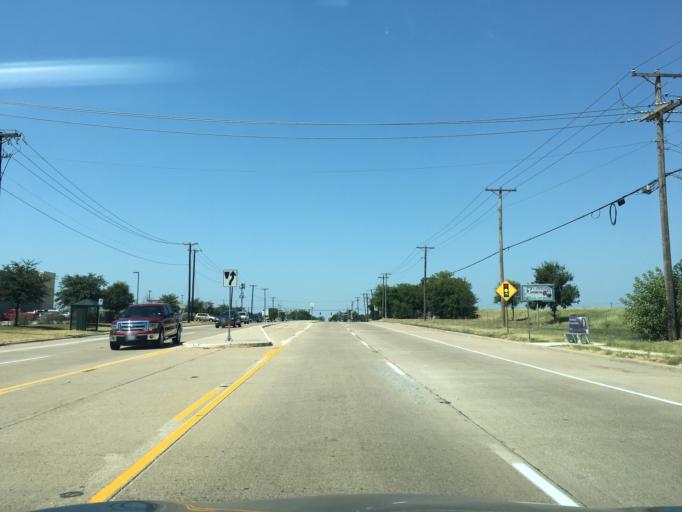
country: US
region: Texas
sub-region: Tarrant County
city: Edgecliff Village
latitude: 32.6322
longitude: -97.3485
